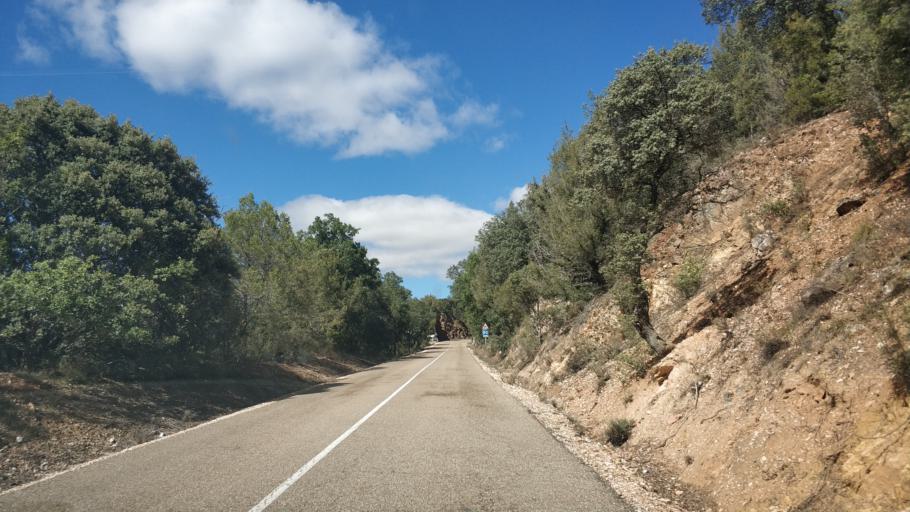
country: ES
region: Castille and Leon
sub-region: Provincia de Burgos
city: Retuerta
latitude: 42.0449
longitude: -3.4695
